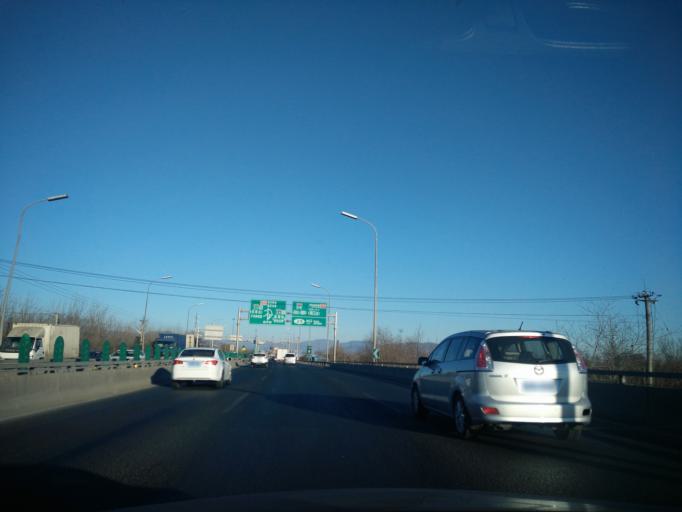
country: CN
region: Beijing
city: Fengtai
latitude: 39.8374
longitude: 116.2260
